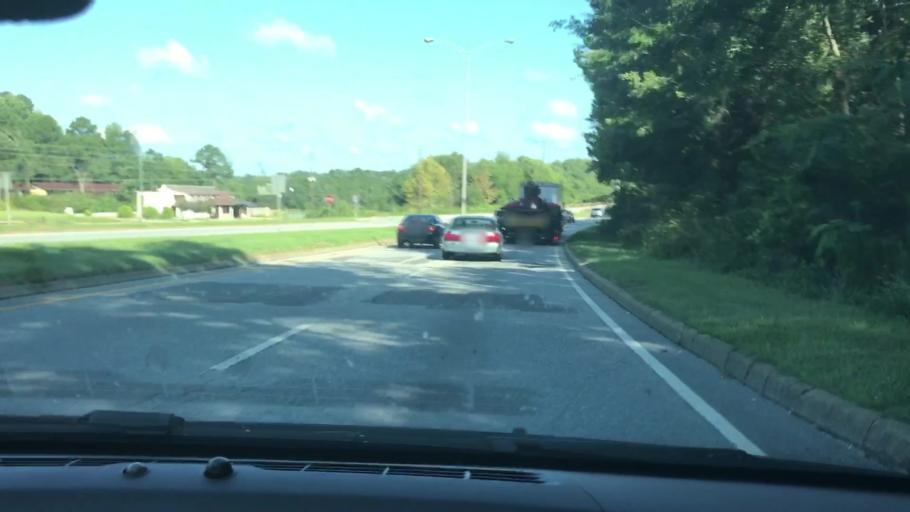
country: US
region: Alabama
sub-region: Barbour County
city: Eufaula
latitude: 31.9051
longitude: -85.1485
